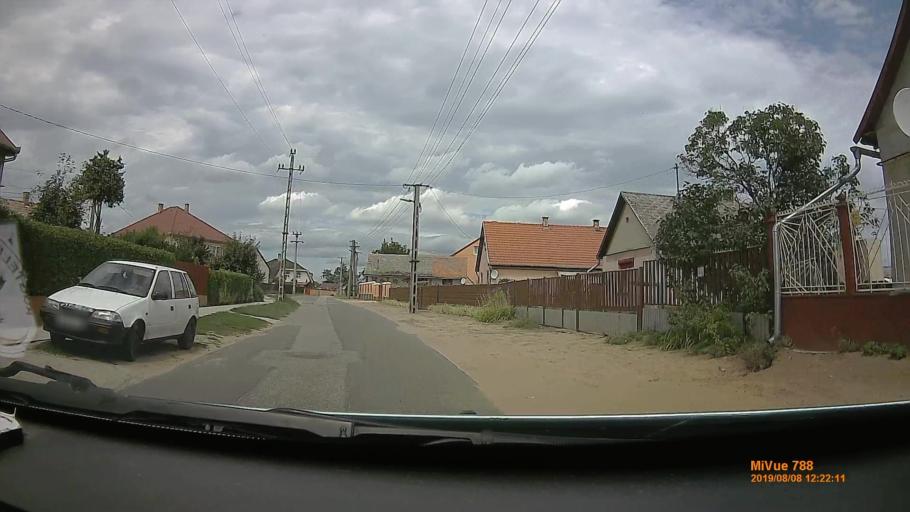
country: HU
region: Szabolcs-Szatmar-Bereg
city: Nyirbogat
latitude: 47.7980
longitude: 22.0545
